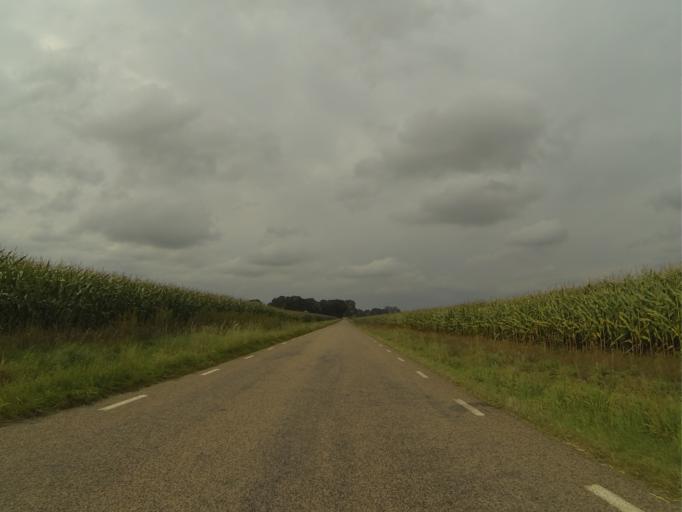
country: SE
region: Skane
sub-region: Eslovs Kommun
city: Eslov
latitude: 55.7651
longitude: 13.2936
